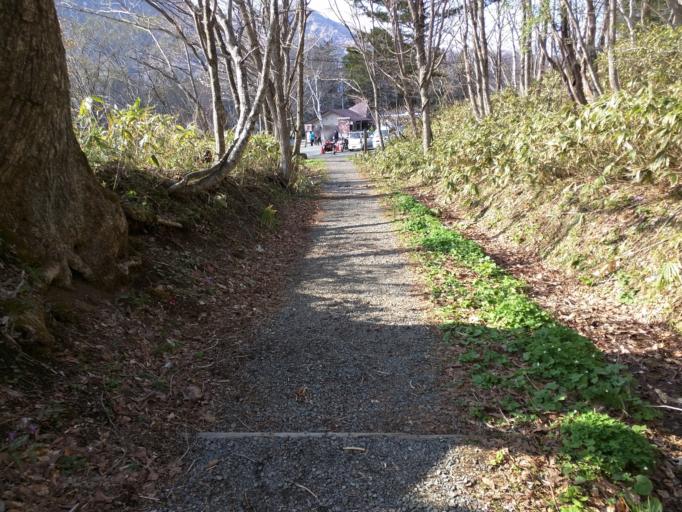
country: JP
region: Nagano
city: Nagano-shi
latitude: 36.7548
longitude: 138.0792
